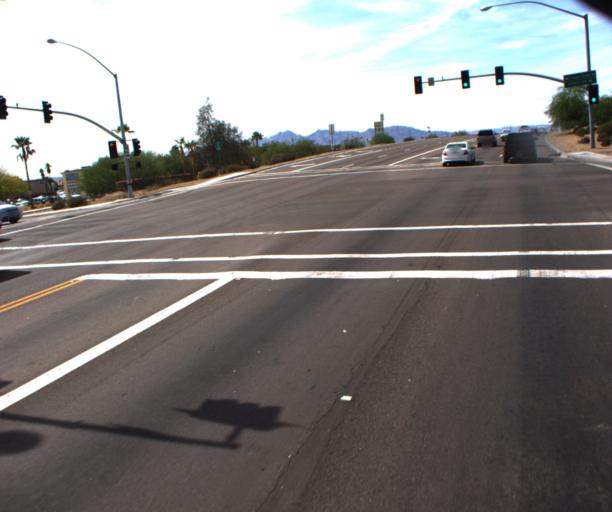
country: US
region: Arizona
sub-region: Mohave County
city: Lake Havasu City
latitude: 34.4745
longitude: -114.3463
